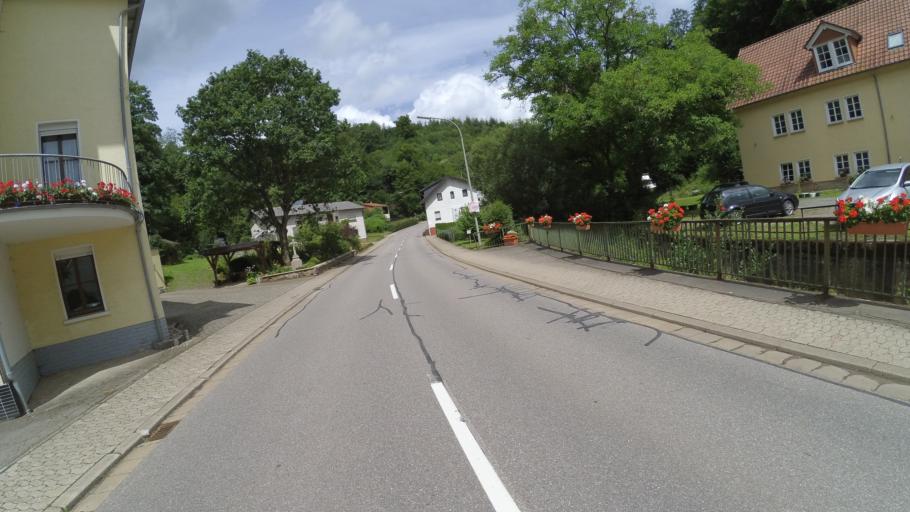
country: DE
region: Saarland
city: Tholey
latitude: 49.4760
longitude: 6.9921
